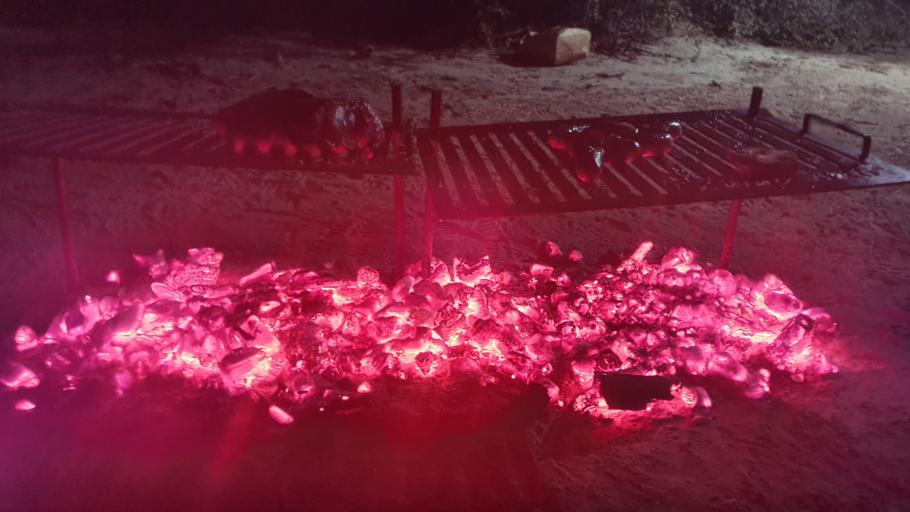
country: BO
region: Chuquisaca
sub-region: Provincia Zudanez
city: Mojocoya
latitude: -18.6709
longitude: -64.5254
